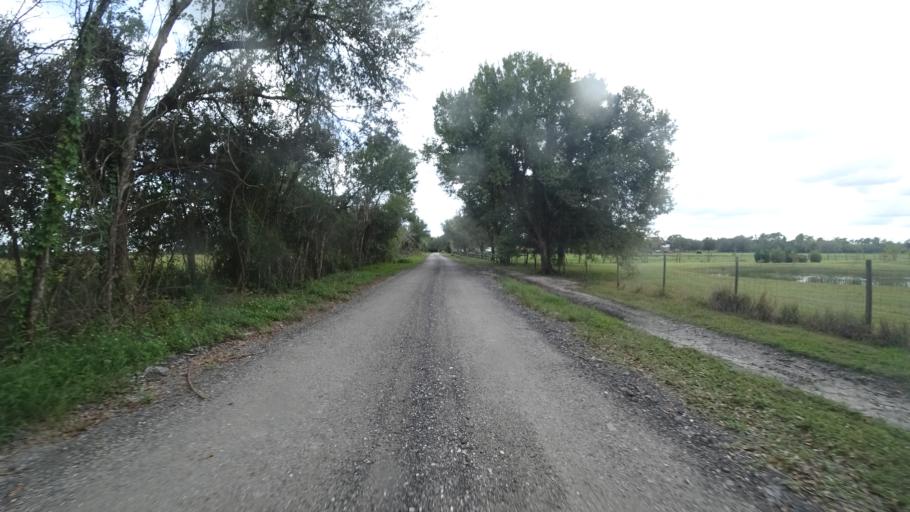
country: US
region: Florida
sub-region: Sarasota County
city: Lake Sarasota
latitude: 27.3965
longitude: -82.2664
